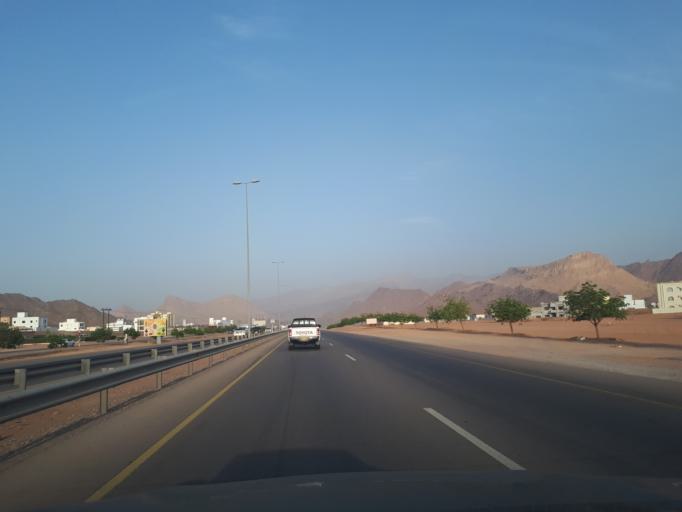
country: OM
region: Muhafazat ad Dakhiliyah
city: Bidbid
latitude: 23.4634
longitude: 58.1556
